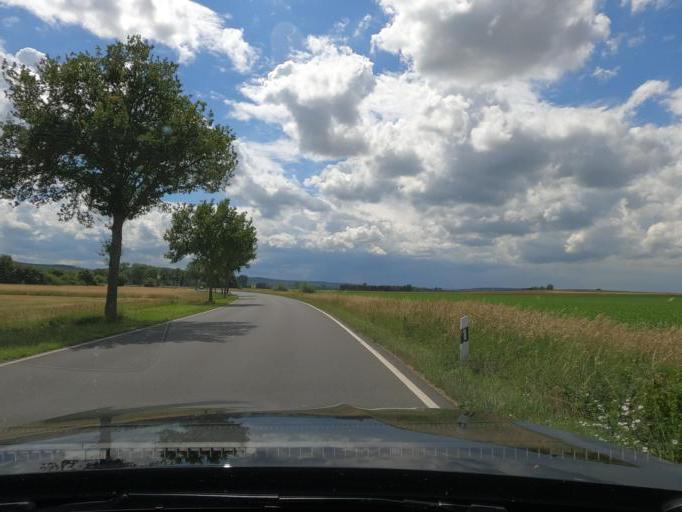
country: DE
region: Lower Saxony
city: Lengede
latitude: 52.1594
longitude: 10.2953
